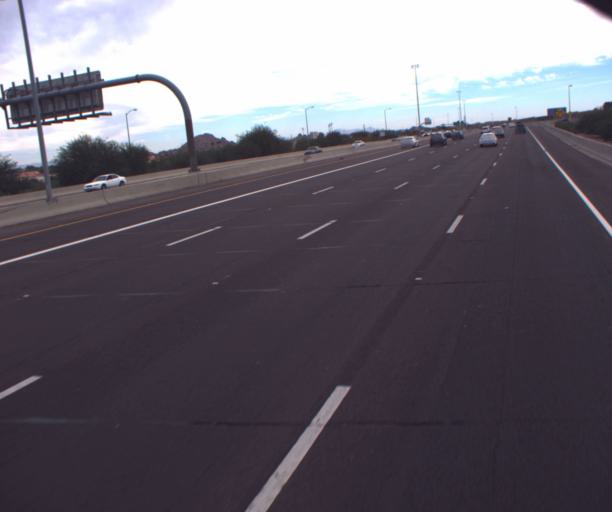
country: US
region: Arizona
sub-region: Maricopa County
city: Phoenix
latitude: 33.4602
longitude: -112.0115
